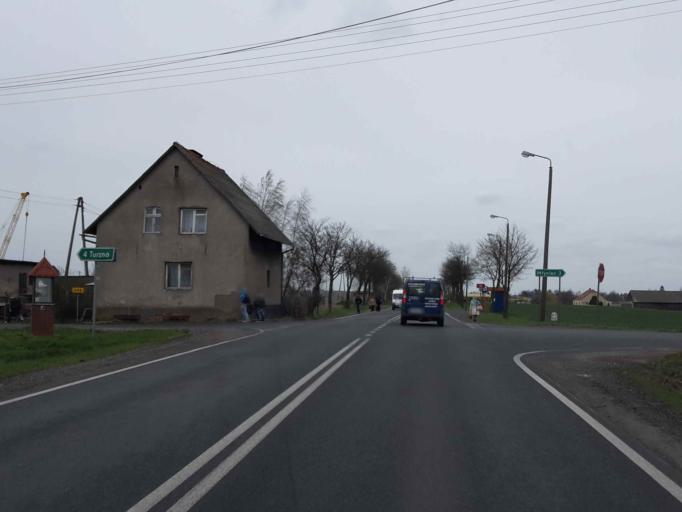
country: PL
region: Kujawsko-Pomorskie
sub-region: Powiat torunski
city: Lubicz Gorny
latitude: 53.0870
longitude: 18.7718
